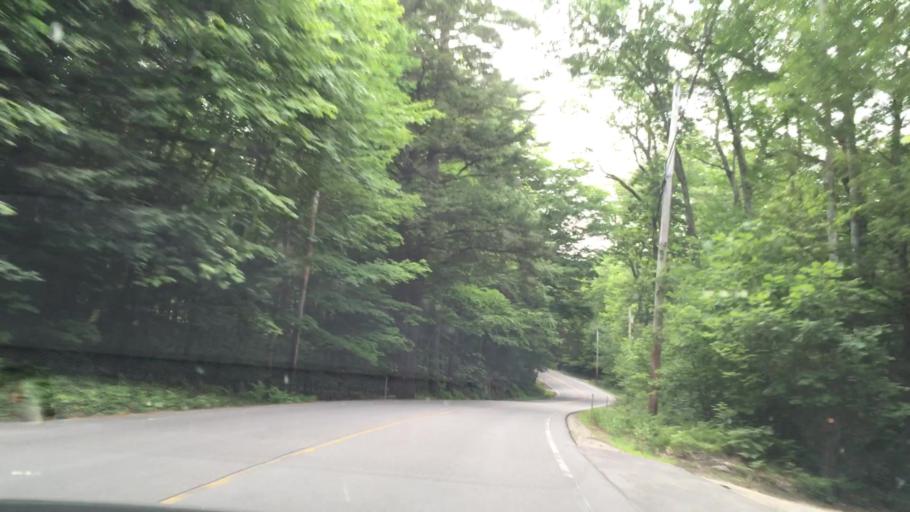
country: US
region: New Hampshire
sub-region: Belknap County
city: Meredith
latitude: 43.7030
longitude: -71.5057
